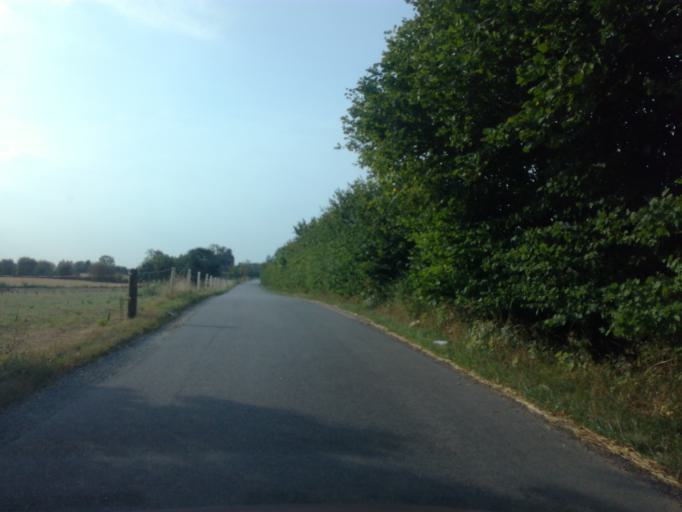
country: DK
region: South Denmark
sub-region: Vejle Kommune
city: Borkop
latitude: 55.6450
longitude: 9.5775
